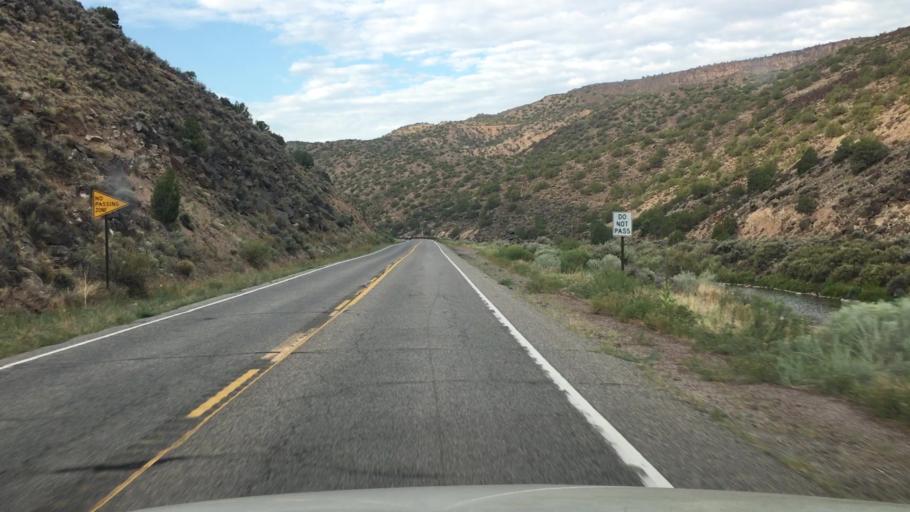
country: US
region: New Mexico
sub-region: Rio Arriba County
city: Ohkay Owingeh
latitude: 36.1946
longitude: -105.9753
